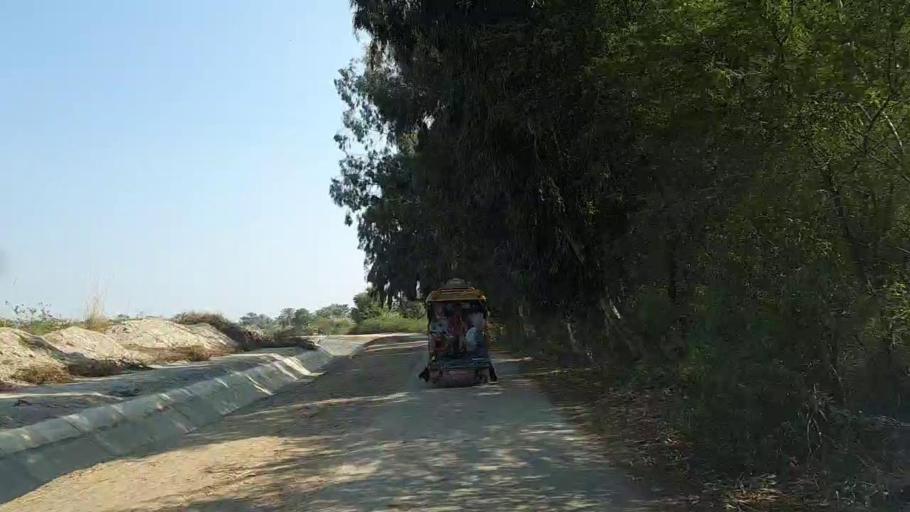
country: PK
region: Sindh
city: Jam Sahib
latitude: 26.2728
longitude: 68.5575
